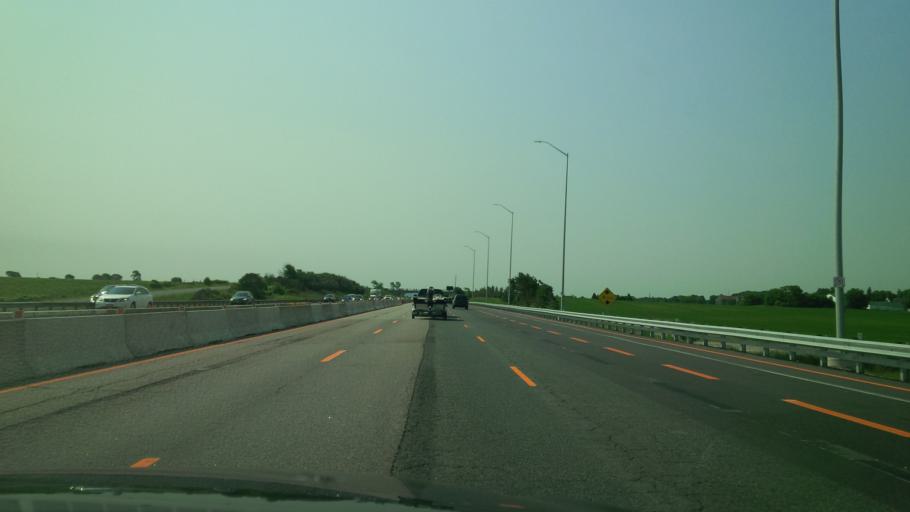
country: CA
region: Ontario
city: Innisfil
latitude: 44.2417
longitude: -79.6682
